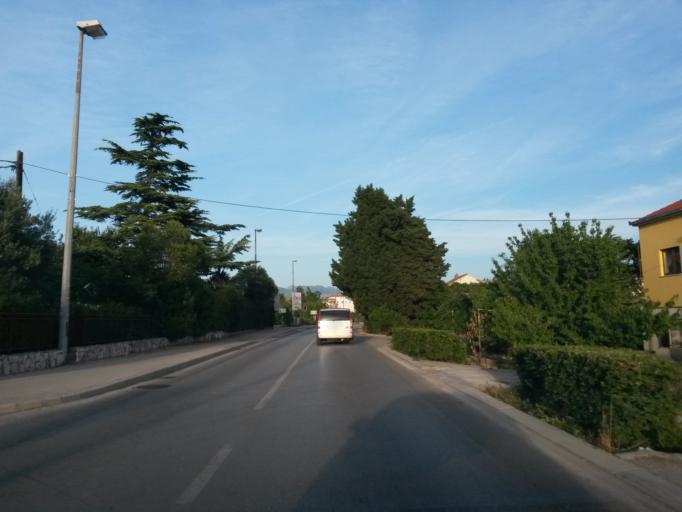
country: HR
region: Splitsko-Dalmatinska
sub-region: Grad Split
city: Split
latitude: 43.5532
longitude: 16.3696
